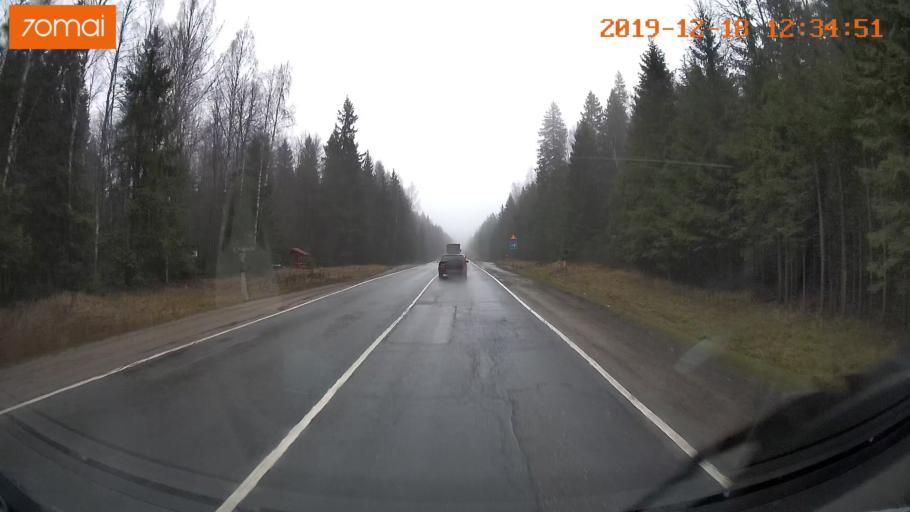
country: RU
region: Moskovskaya
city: Rumyantsevo
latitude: 56.1245
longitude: 36.5767
